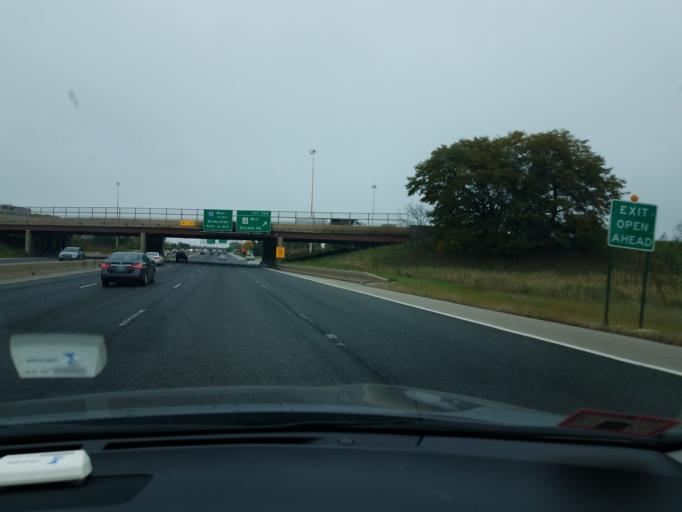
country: US
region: Illinois
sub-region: Cook County
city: Glencoe
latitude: 42.1372
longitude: -87.7874
